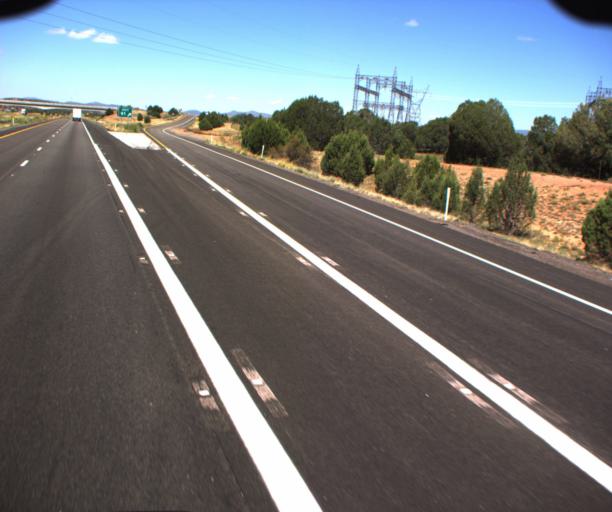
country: US
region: Arizona
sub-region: Mohave County
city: Peach Springs
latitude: 35.1910
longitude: -113.3609
